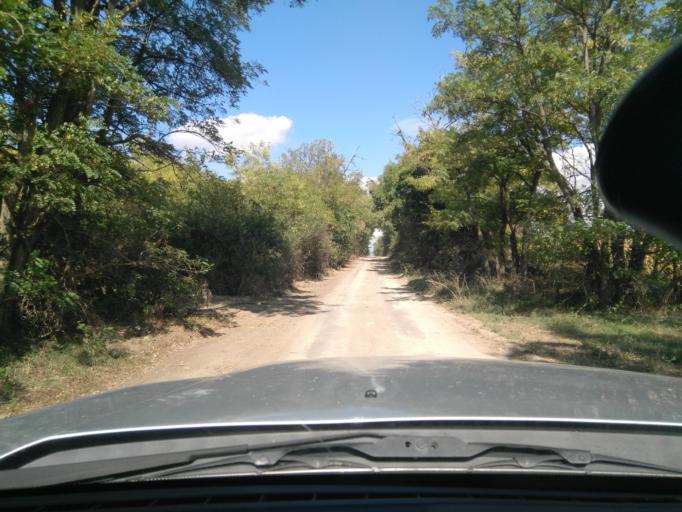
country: HU
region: Fejer
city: Bicske
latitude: 47.4365
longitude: 18.6420
